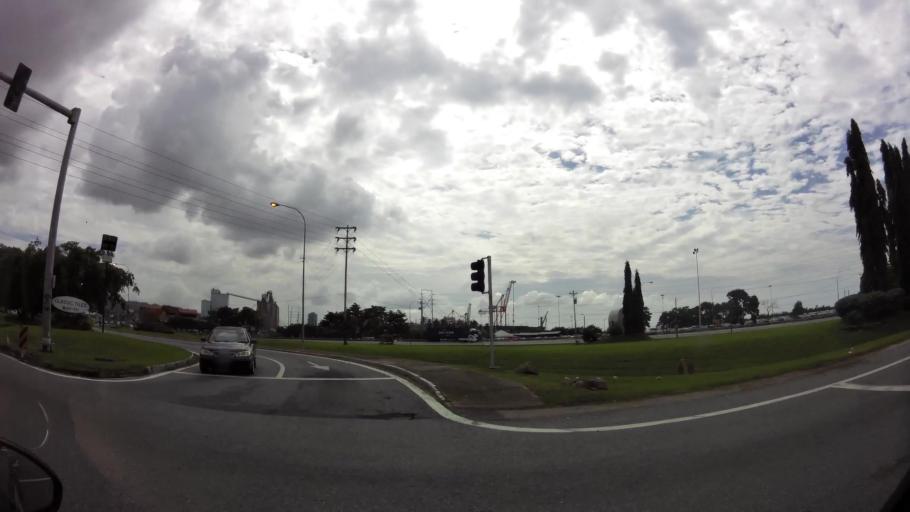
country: TT
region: City of Port of Spain
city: Mucurapo
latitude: 10.6604
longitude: -61.5303
